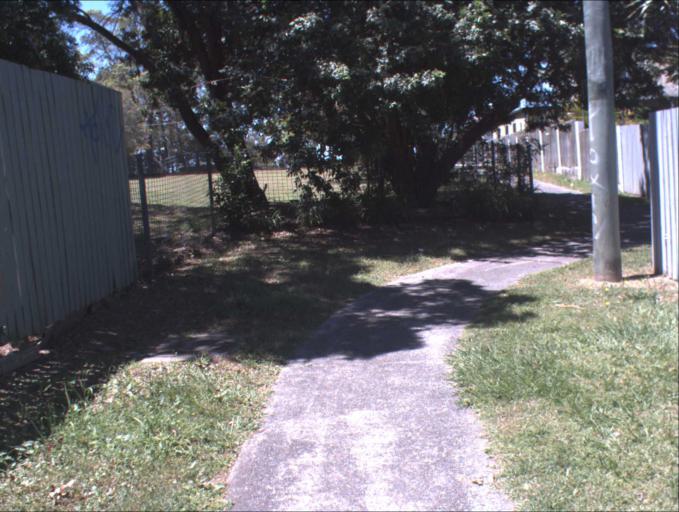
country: AU
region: Queensland
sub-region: Logan
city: Logan City
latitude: -27.6404
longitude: 153.1259
